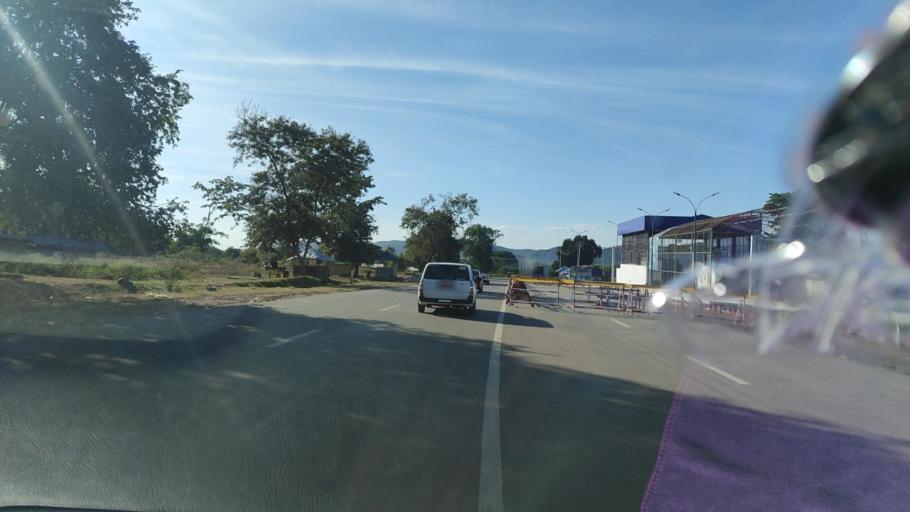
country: MM
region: Mandalay
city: Yamethin
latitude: 20.7509
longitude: 96.2741
